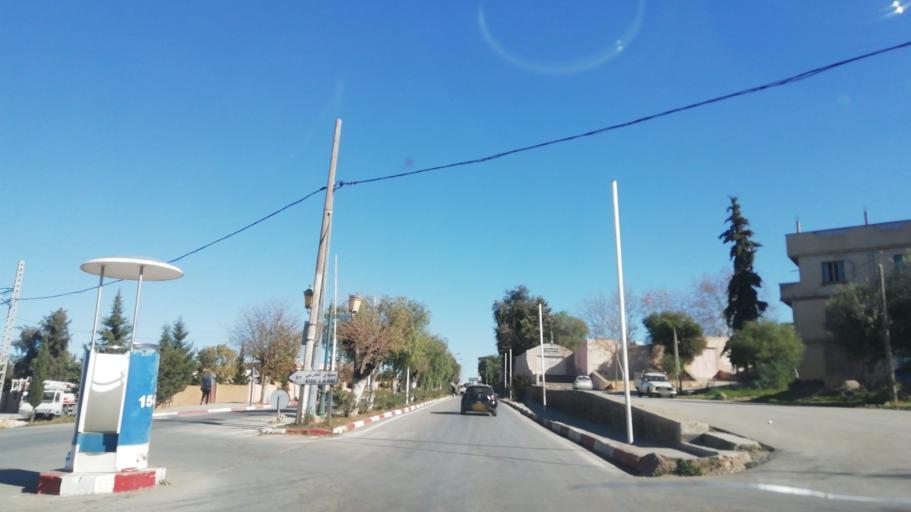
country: DZ
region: Tlemcen
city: Beni Mester
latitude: 34.8314
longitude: -1.5188
